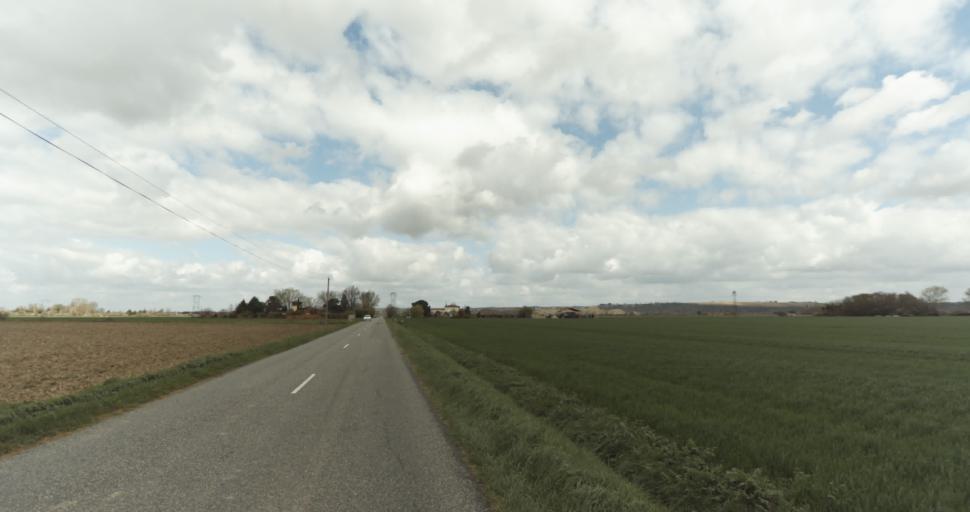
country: FR
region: Midi-Pyrenees
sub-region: Departement de la Haute-Garonne
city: Auterive
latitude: 43.3185
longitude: 1.4750
